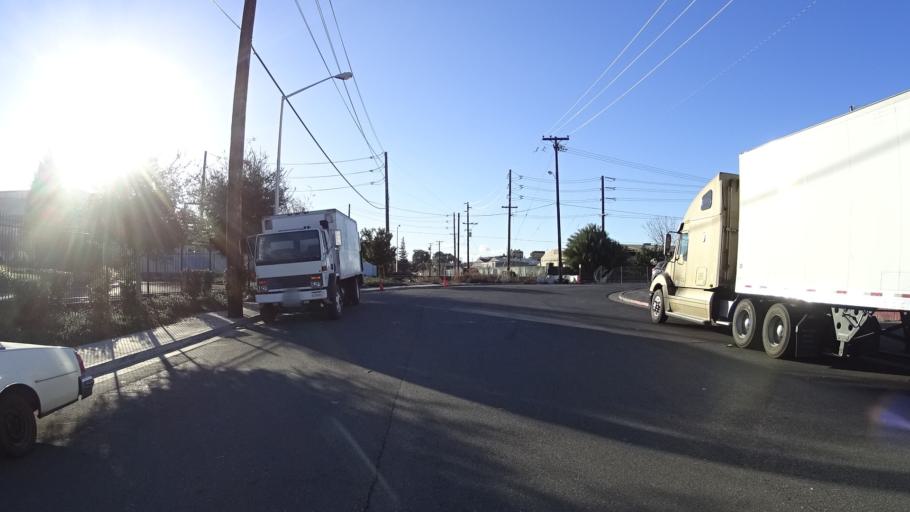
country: US
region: California
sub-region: Santa Clara County
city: Santa Clara
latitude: 37.3634
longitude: -121.9448
